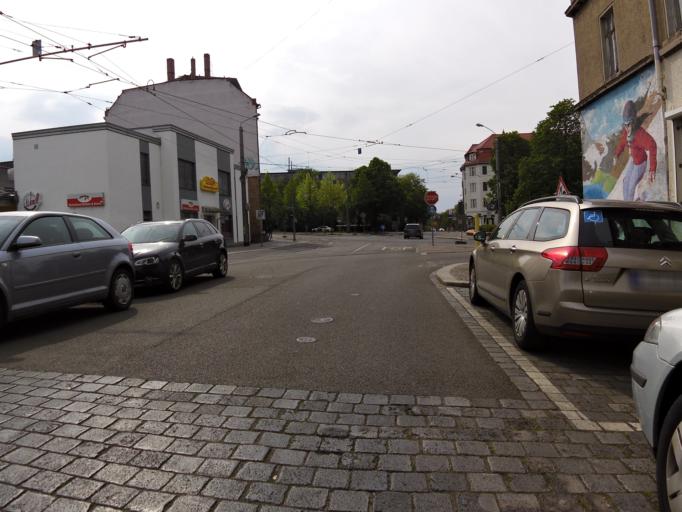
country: DE
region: Saxony
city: Leipzig
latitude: 51.3514
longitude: 12.4084
